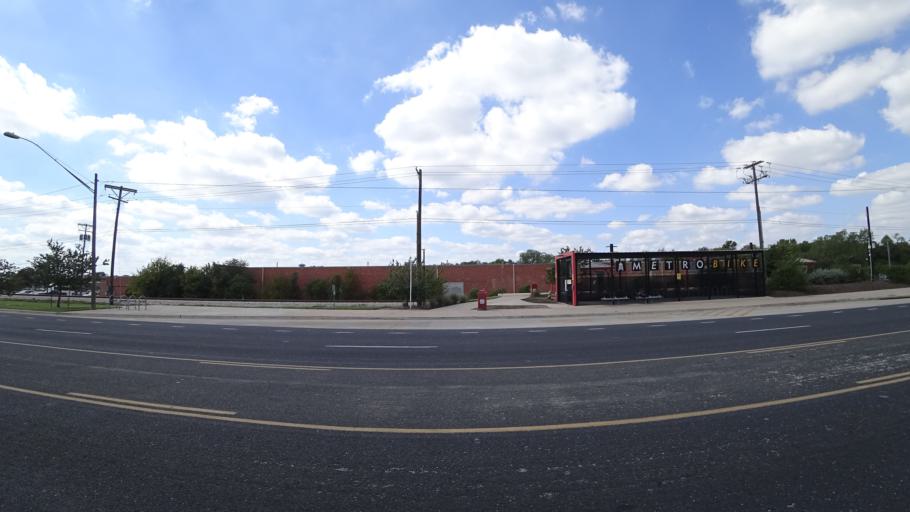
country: US
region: Texas
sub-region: Travis County
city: Austin
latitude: 30.3284
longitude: -97.7158
